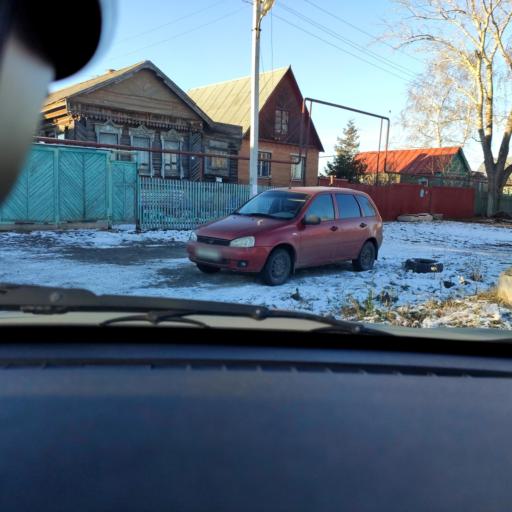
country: RU
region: Samara
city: Tol'yatti
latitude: 53.5581
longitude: 49.3981
